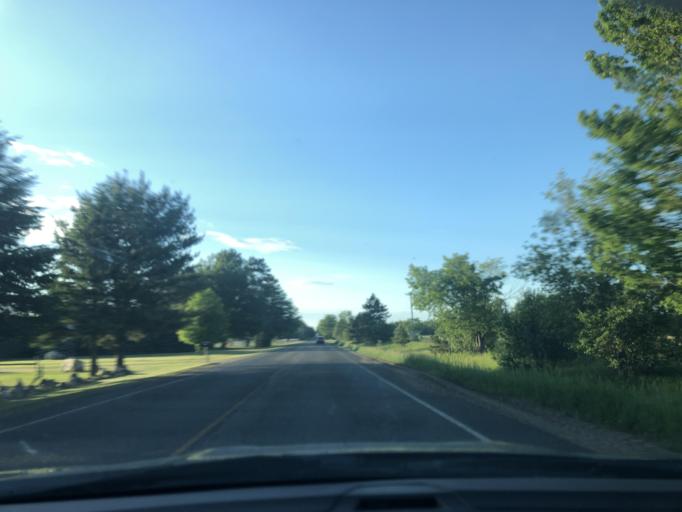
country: US
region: Michigan
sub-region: Missaukee County
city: Lake City
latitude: 44.3805
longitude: -85.0758
